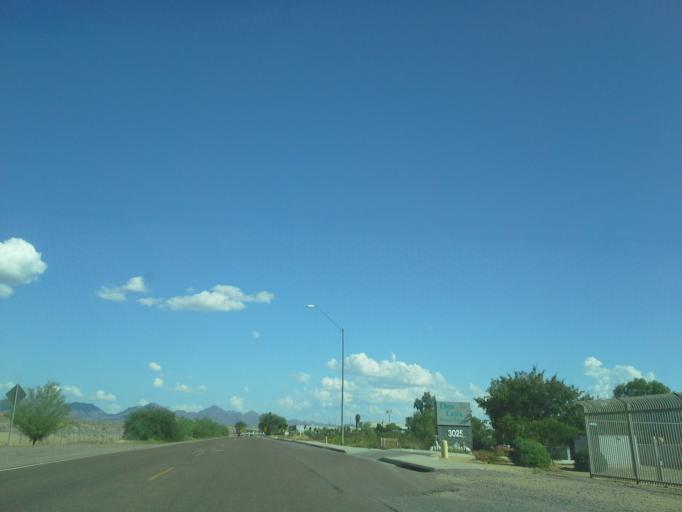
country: US
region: Arizona
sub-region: Maricopa County
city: Paradise Valley
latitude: 33.6766
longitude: -112.0184
